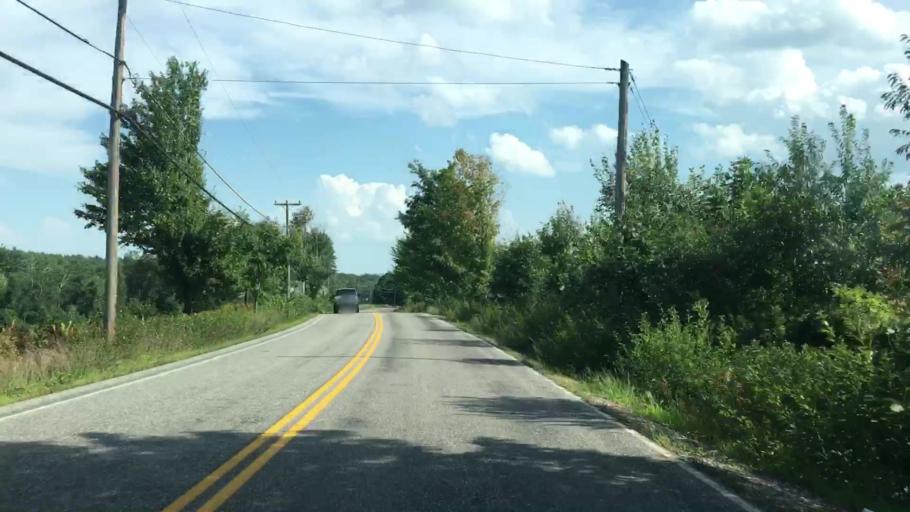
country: US
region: New Hampshire
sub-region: Belknap County
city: Sanbornton
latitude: 43.4857
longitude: -71.5801
